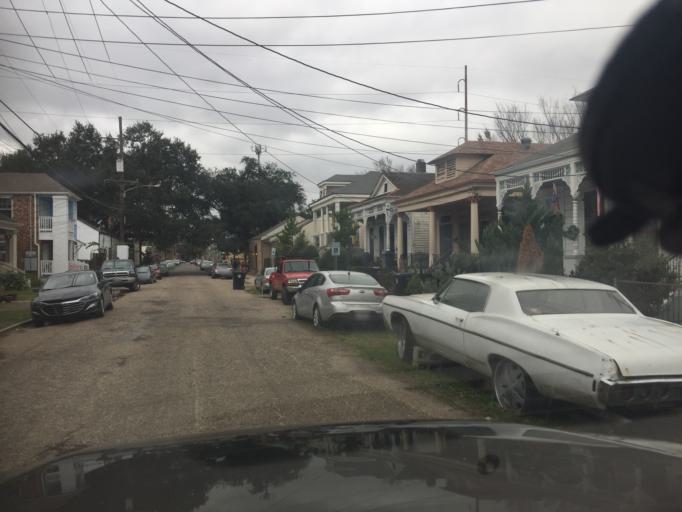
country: US
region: Louisiana
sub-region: Orleans Parish
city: New Orleans
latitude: 29.9762
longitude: -90.0746
